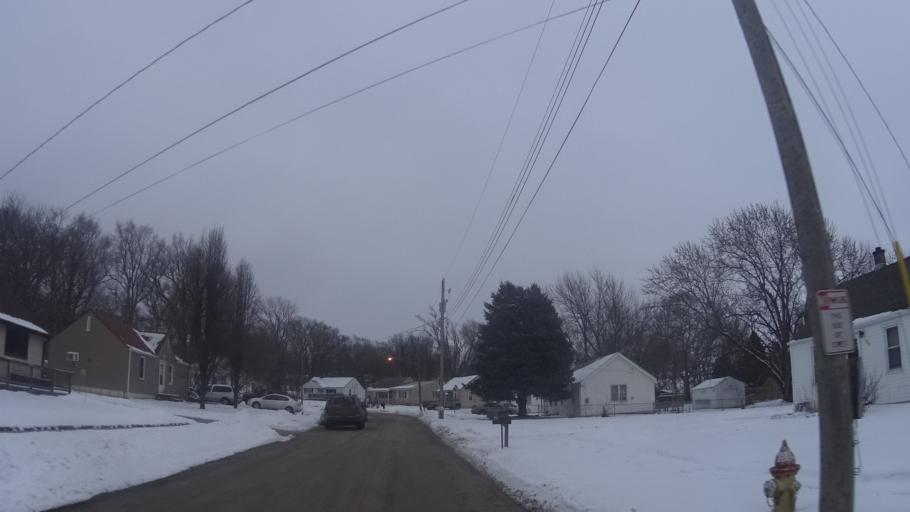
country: US
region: Nebraska
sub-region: Sarpy County
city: Offutt Air Force Base
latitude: 41.1362
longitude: -95.9235
